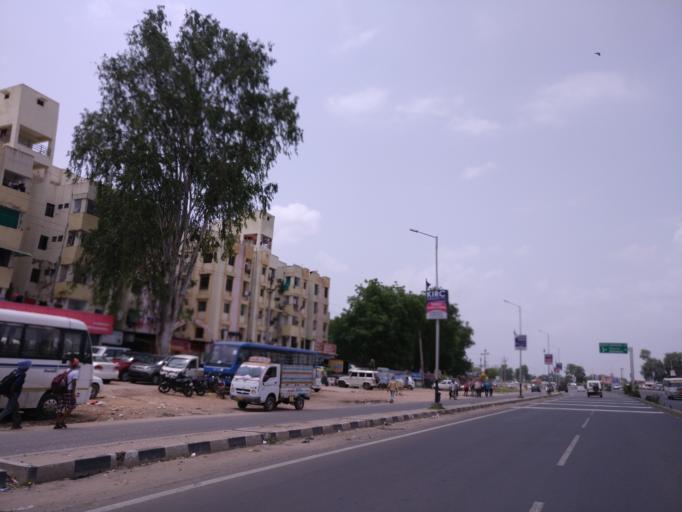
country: IN
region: Gujarat
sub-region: Mahesana
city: Jhulasan
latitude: 23.2502
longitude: 72.4854
